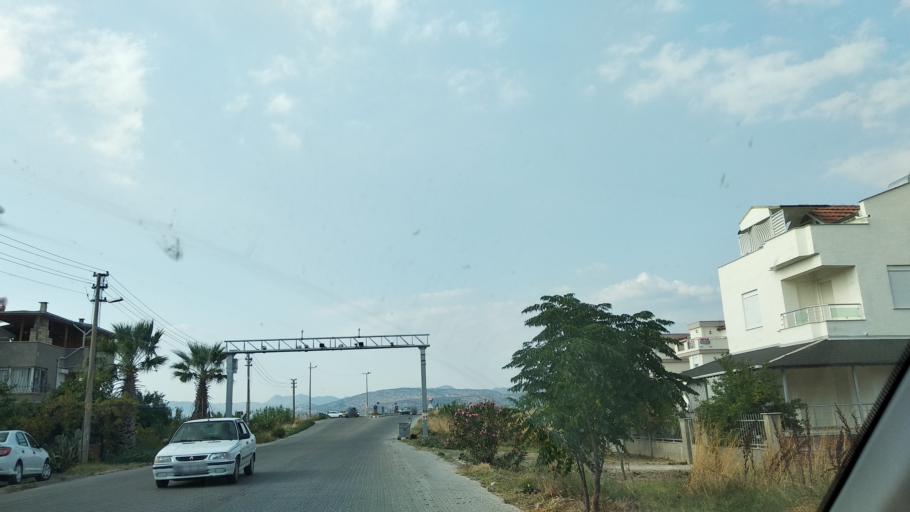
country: TR
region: Izmir
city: Dikili
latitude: 39.1031
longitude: 26.8828
